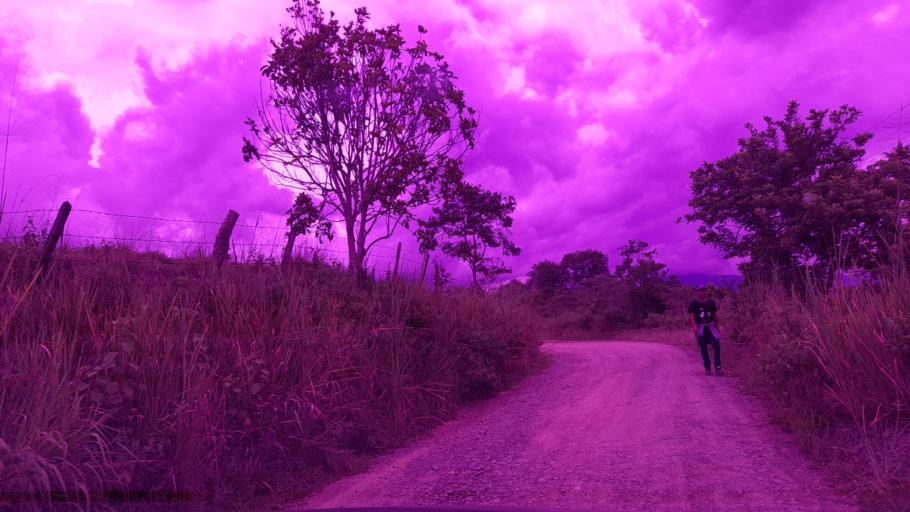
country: CO
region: Valle del Cauca
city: Bugalagrande
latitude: 4.1886
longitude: -76.1388
